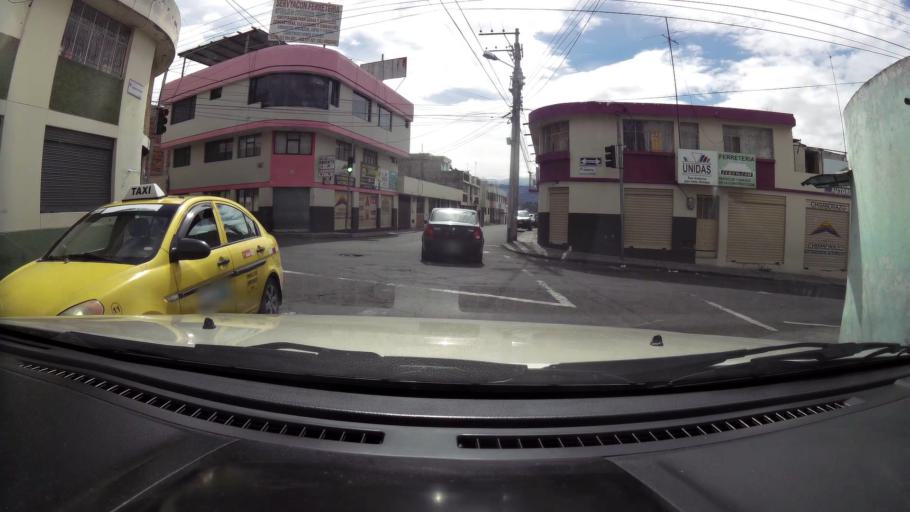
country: EC
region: Cotopaxi
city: Latacunga
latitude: -0.9279
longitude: -78.6118
